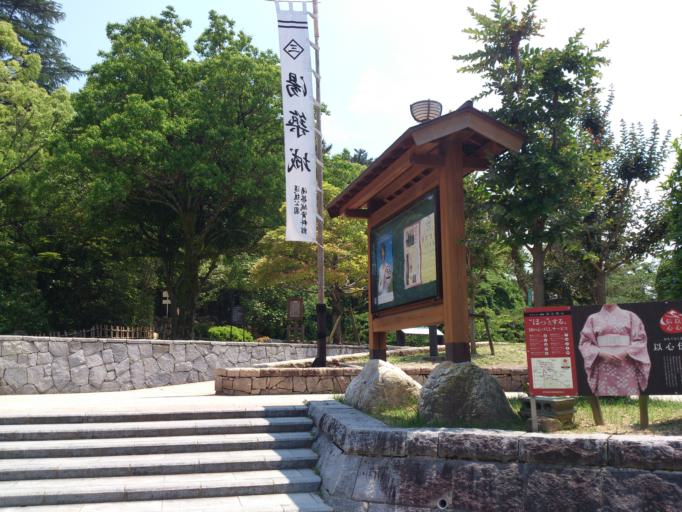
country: JP
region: Ehime
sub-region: Shikoku-chuo Shi
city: Matsuyama
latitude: 33.8500
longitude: 132.7861
